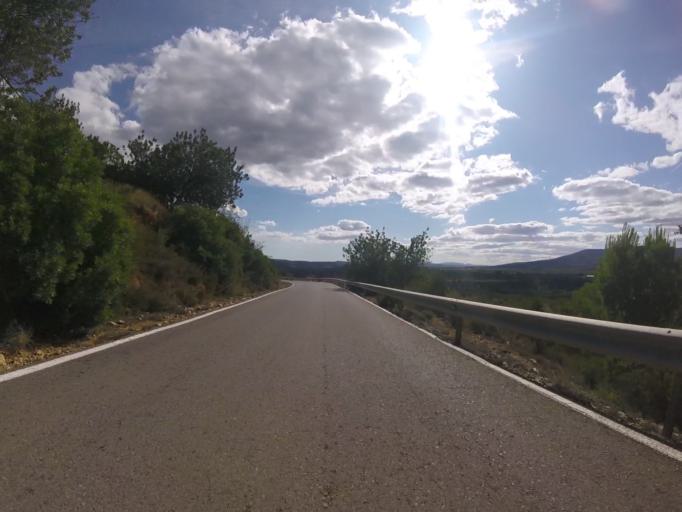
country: ES
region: Valencia
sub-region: Provincia de Castello
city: Cuevas de Vinroma
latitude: 40.3695
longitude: 0.1180
